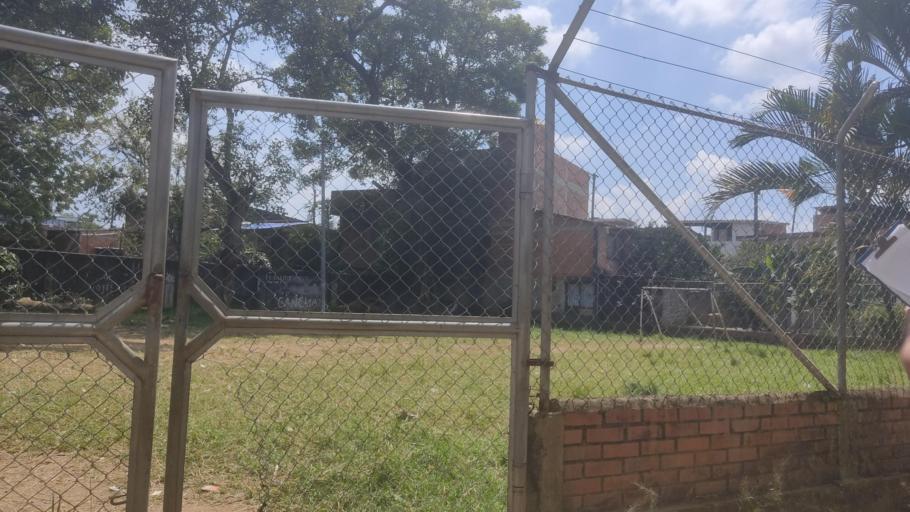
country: CO
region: Valle del Cauca
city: Jamundi
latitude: 3.2499
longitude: -76.5434
